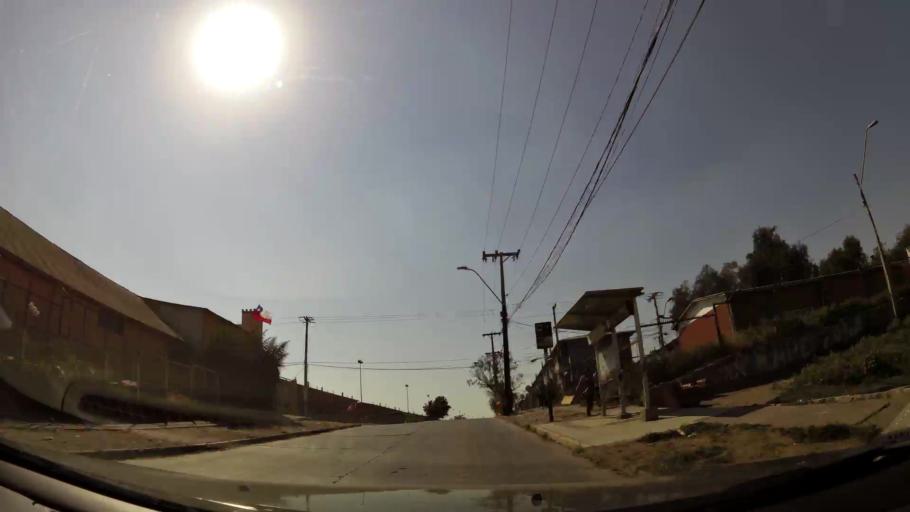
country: CL
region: Santiago Metropolitan
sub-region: Provincia de Cordillera
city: Puente Alto
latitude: -33.6288
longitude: -70.6194
